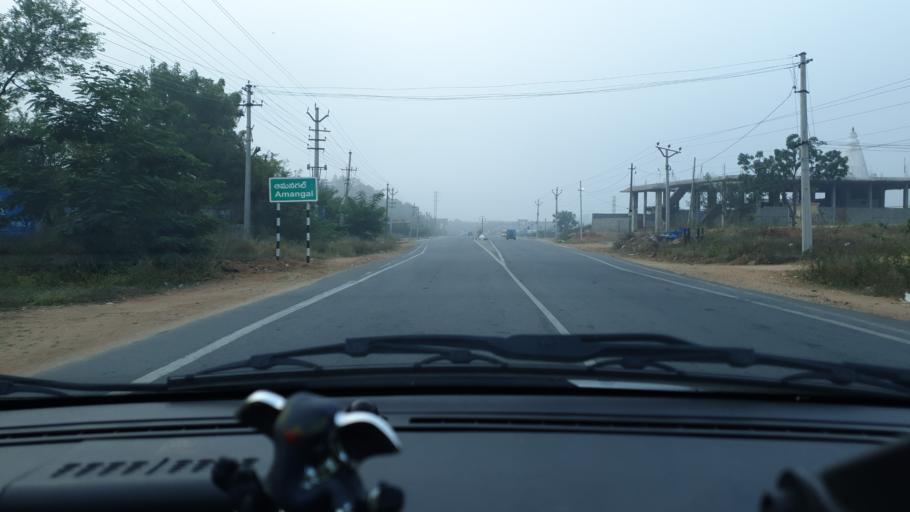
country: IN
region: Telangana
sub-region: Mahbubnagar
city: Farrukhnagar
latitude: 16.8643
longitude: 78.5287
